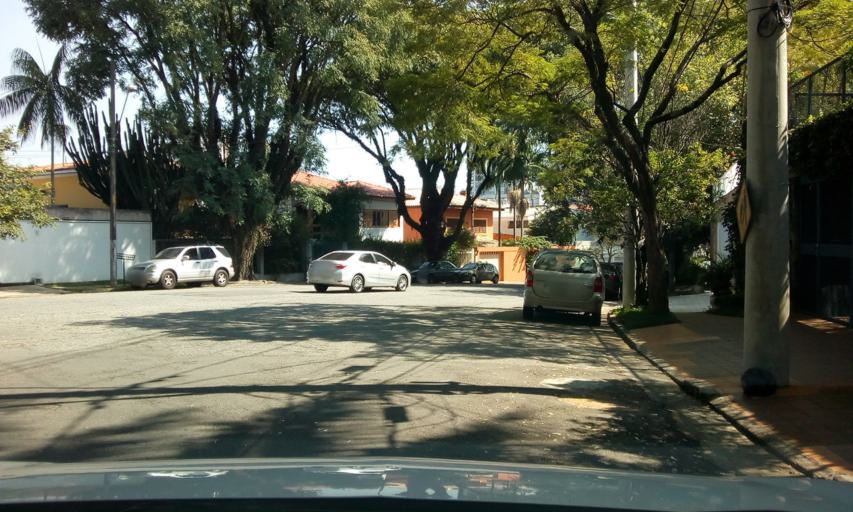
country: BR
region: Sao Paulo
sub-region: Sao Paulo
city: Sao Paulo
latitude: -23.5463
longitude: -46.6830
